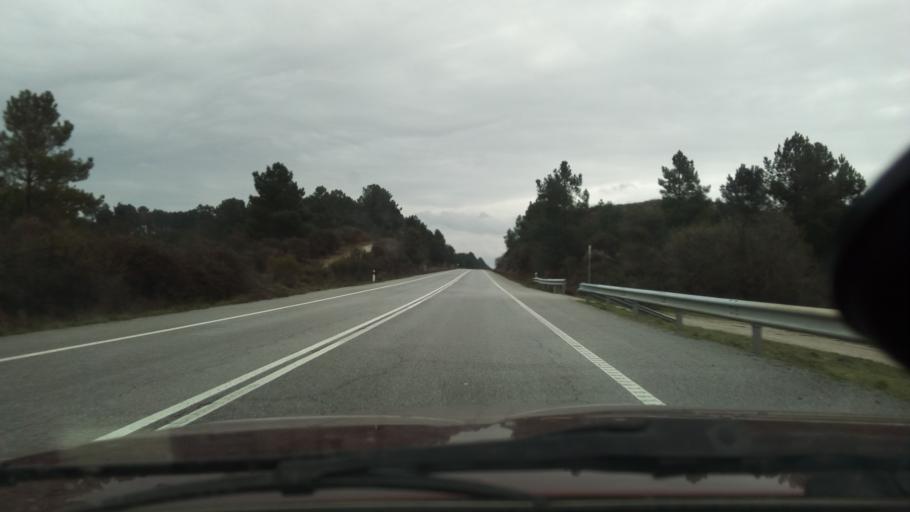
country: PT
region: Guarda
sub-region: Fornos de Algodres
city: Fornos de Algodres
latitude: 40.6028
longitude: -7.5779
